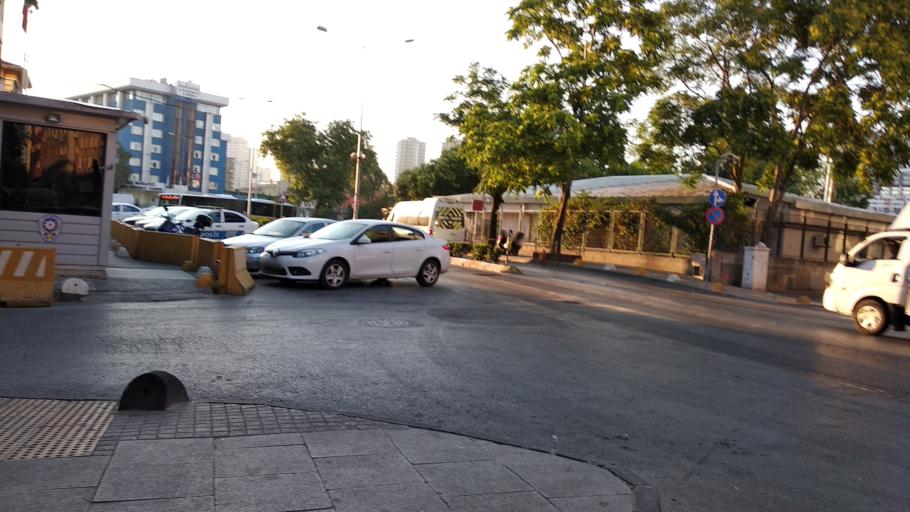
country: TR
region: Istanbul
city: UEskuedar
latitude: 40.9950
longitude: 29.0413
